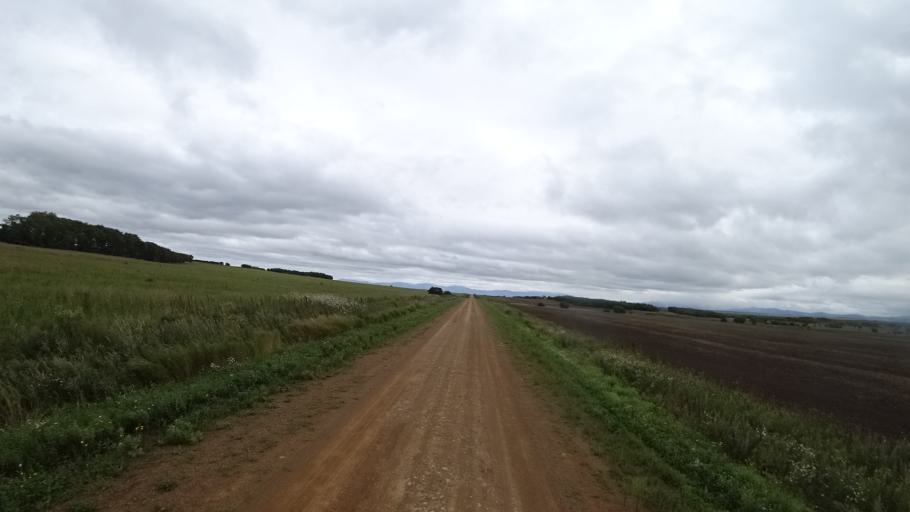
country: RU
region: Primorskiy
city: Chernigovka
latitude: 44.4371
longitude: 132.5814
